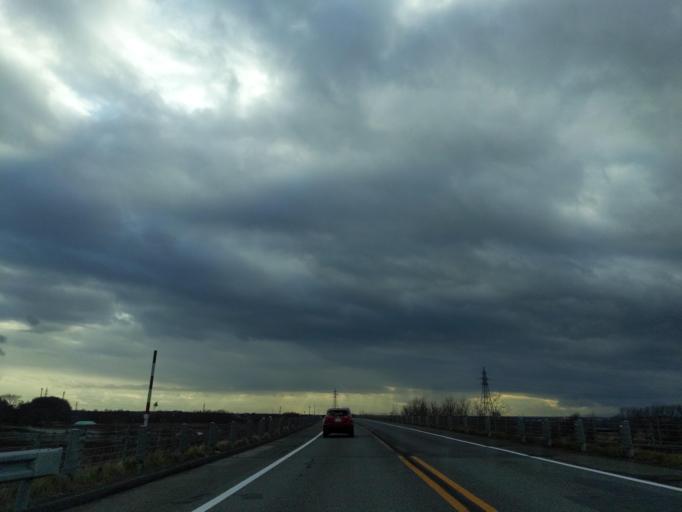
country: JP
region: Hokkaido
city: Chitose
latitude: 42.8427
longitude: 141.6950
